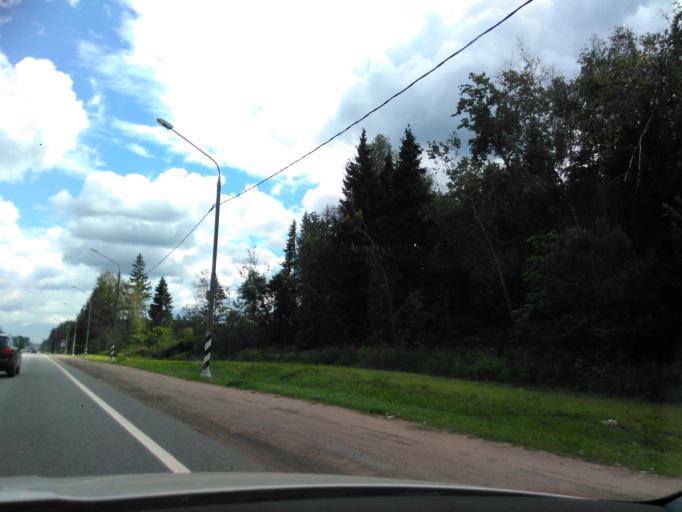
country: RU
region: Moskovskaya
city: Shevlyakovo
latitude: 56.2650
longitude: 36.8523
